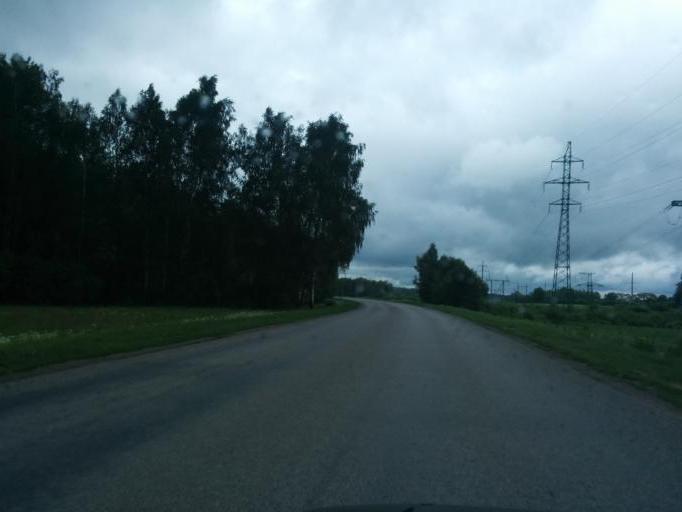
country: LV
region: Valmieras Rajons
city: Valmiera
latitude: 57.5122
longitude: 25.4530
